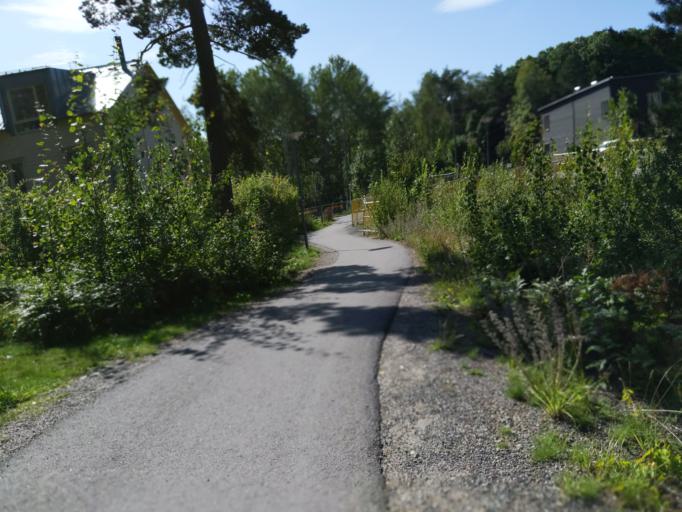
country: SE
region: Stockholm
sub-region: Solna Kommun
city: Rasunda
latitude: 59.3839
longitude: 17.9739
